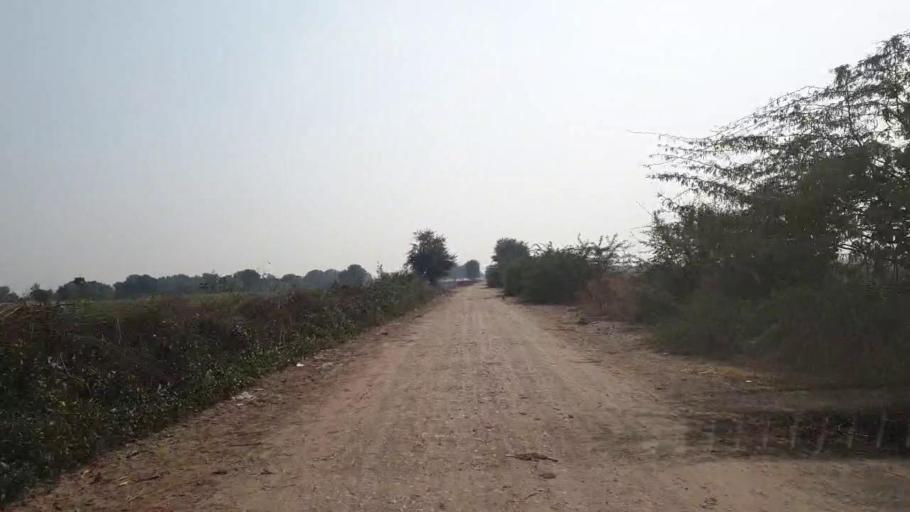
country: PK
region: Sindh
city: Hala
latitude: 25.8325
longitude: 68.4478
